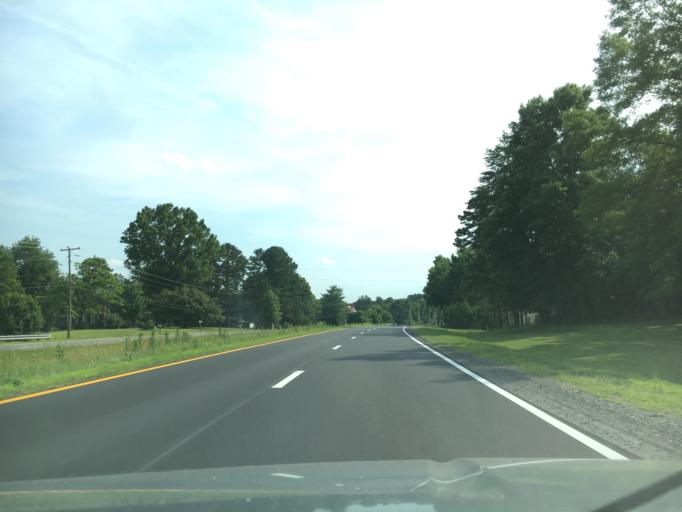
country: US
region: Virginia
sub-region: Halifax County
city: Halifax
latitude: 36.8112
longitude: -78.7533
